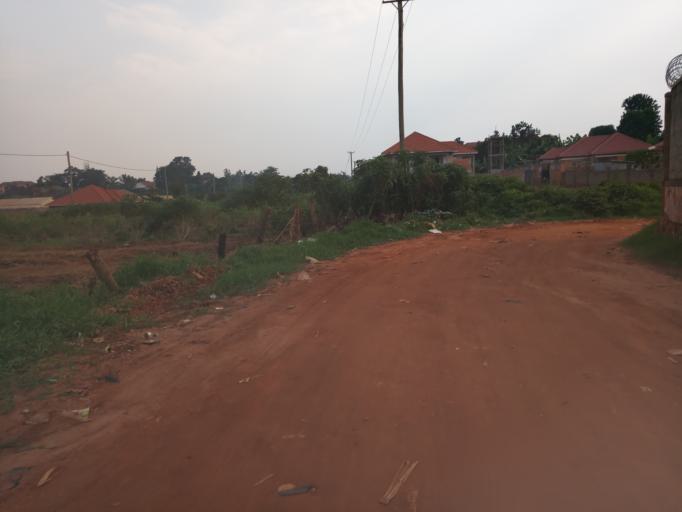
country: UG
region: Central Region
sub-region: Wakiso District
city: Kireka
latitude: 0.3895
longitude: 32.6379
